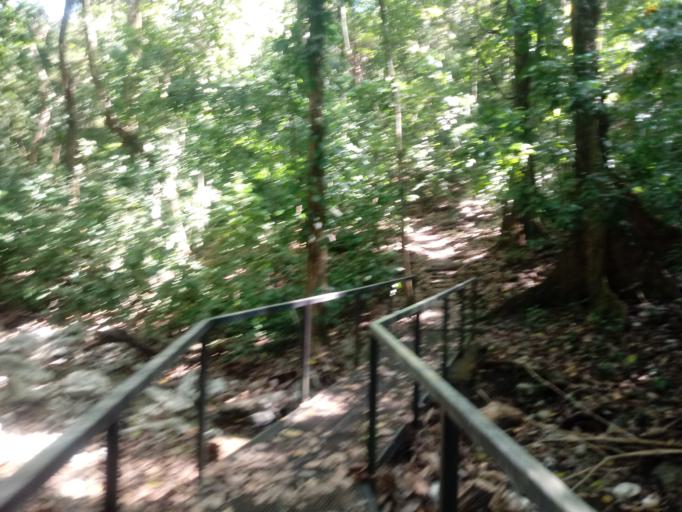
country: CR
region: Puntarenas
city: Paquera
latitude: 9.5832
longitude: -85.1004
